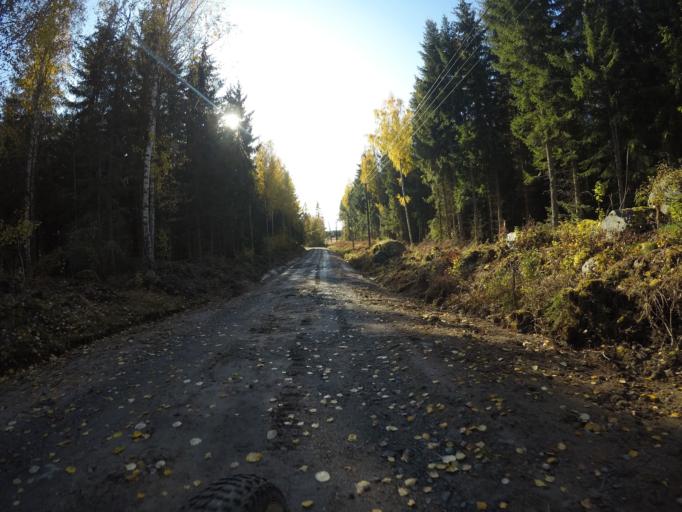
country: SE
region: Vaestmanland
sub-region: Kungsors Kommun
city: Kungsoer
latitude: 59.3127
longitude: 16.0977
